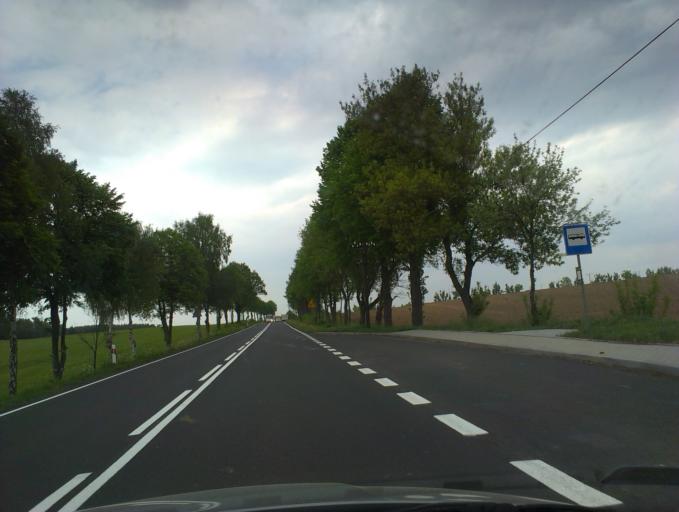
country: PL
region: West Pomeranian Voivodeship
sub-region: Powiat szczecinecki
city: Szczecinek
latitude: 53.8035
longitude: 16.6408
